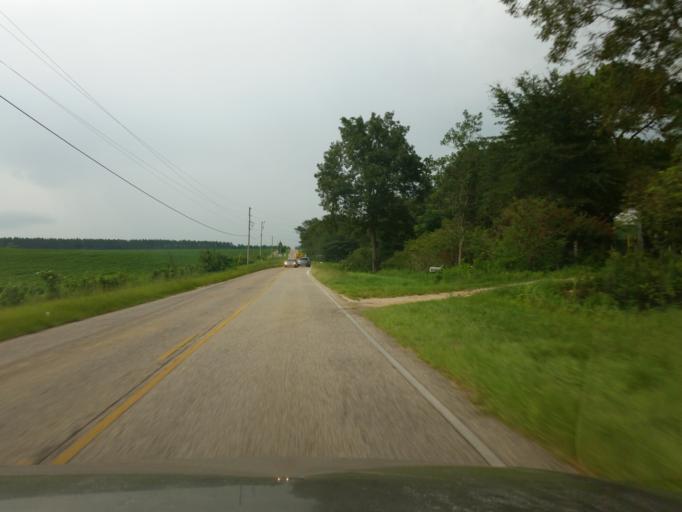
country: US
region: Alabama
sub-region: Baldwin County
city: Robertsdale
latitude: 30.5697
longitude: -87.5815
